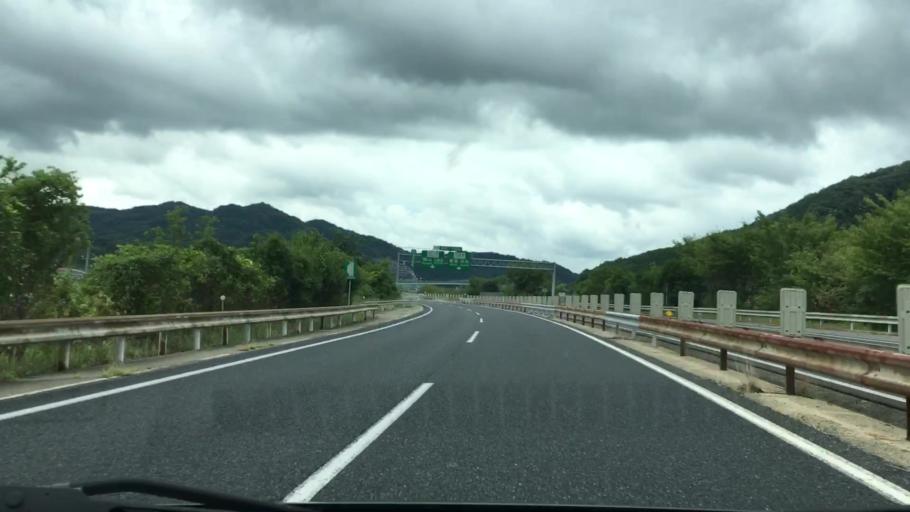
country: JP
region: Okayama
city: Takahashi
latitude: 34.9897
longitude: 133.6902
